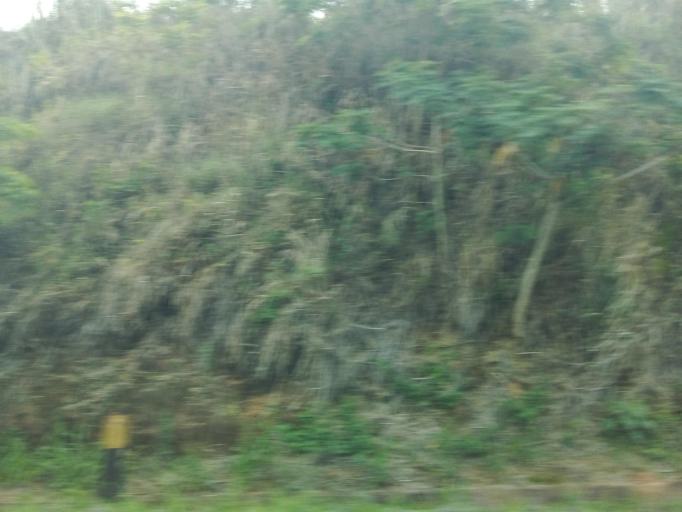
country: BR
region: Minas Gerais
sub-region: Governador Valadares
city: Governador Valadares
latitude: -19.0695
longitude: -42.1510
